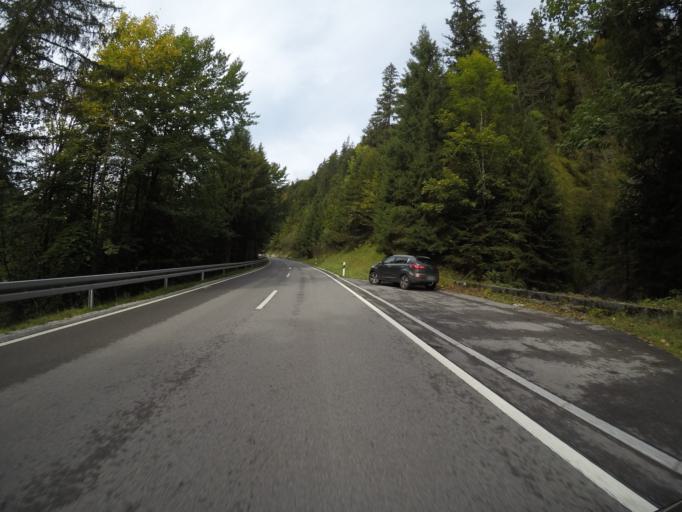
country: DE
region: Bavaria
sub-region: Upper Bavaria
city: Lenggries
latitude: 47.5847
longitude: 11.5775
